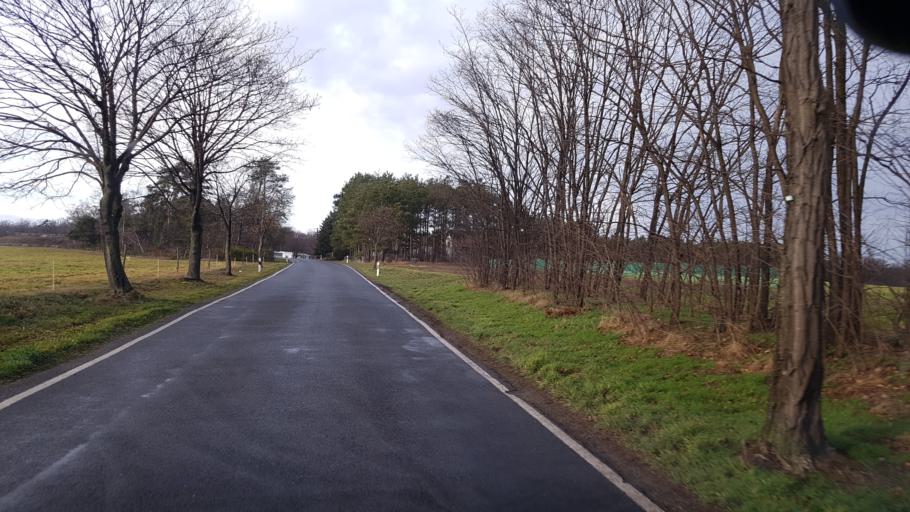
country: DE
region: Brandenburg
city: Altdobern
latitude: 51.6666
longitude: 13.9915
